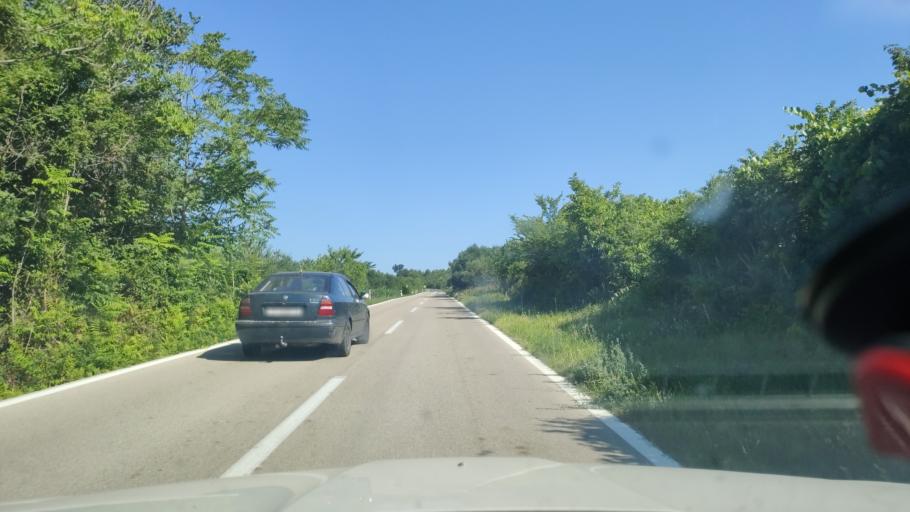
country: HR
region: Sibensko-Kniniska
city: Zaton
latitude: 43.8665
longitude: 15.8879
